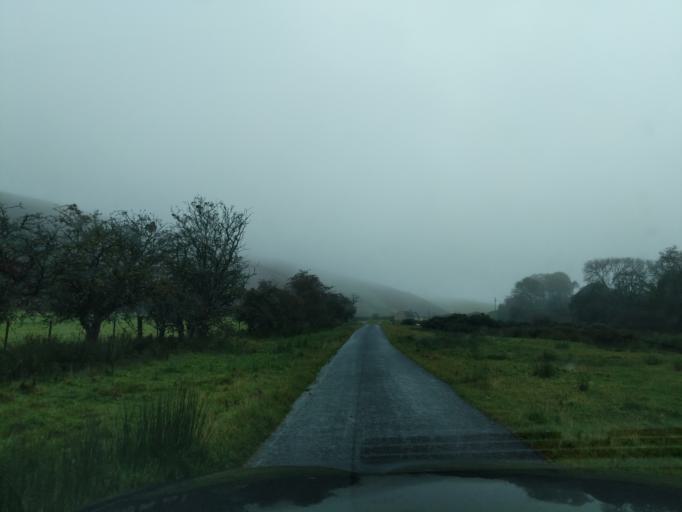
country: GB
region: Scotland
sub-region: East Lothian
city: Dunbar
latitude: 55.9276
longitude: -2.4294
